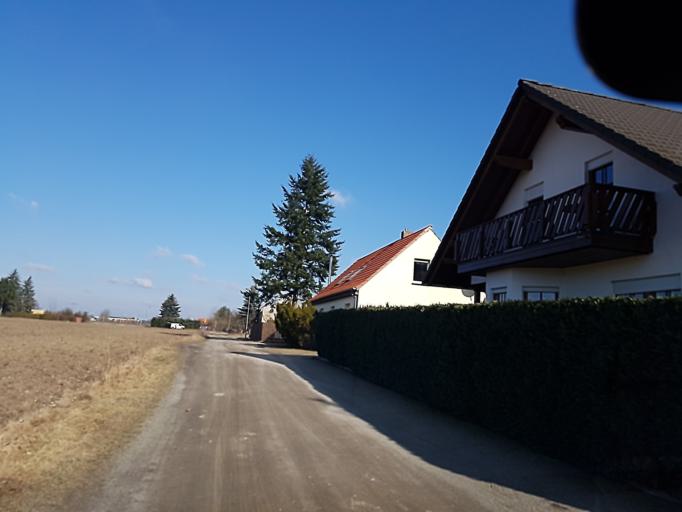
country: DE
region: Brandenburg
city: Doberlug-Kirchhain
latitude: 51.6074
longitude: 13.5618
